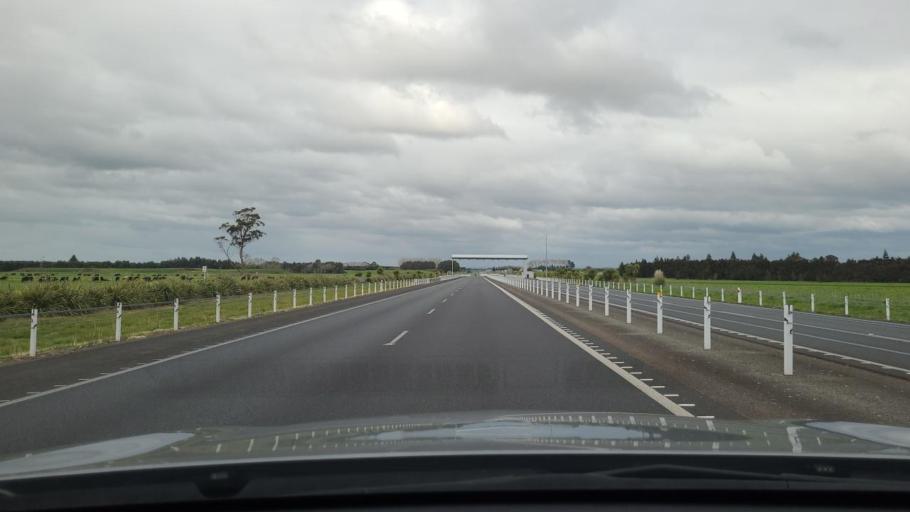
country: NZ
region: Bay of Plenty
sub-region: Western Bay of Plenty District
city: Maketu
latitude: -37.7727
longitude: 176.3793
